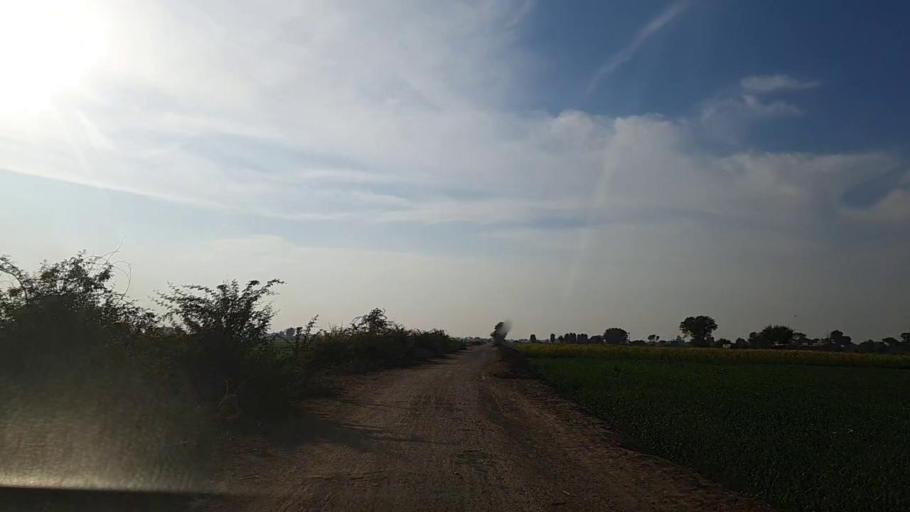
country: PK
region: Sindh
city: Bandhi
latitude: 26.5531
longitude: 68.2629
